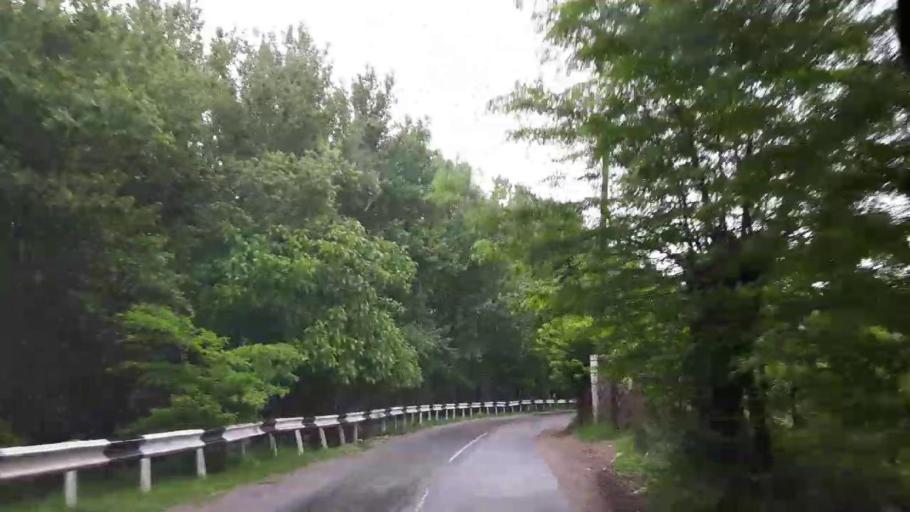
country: GE
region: Shida Kartli
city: Gori
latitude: 41.9660
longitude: 44.2182
